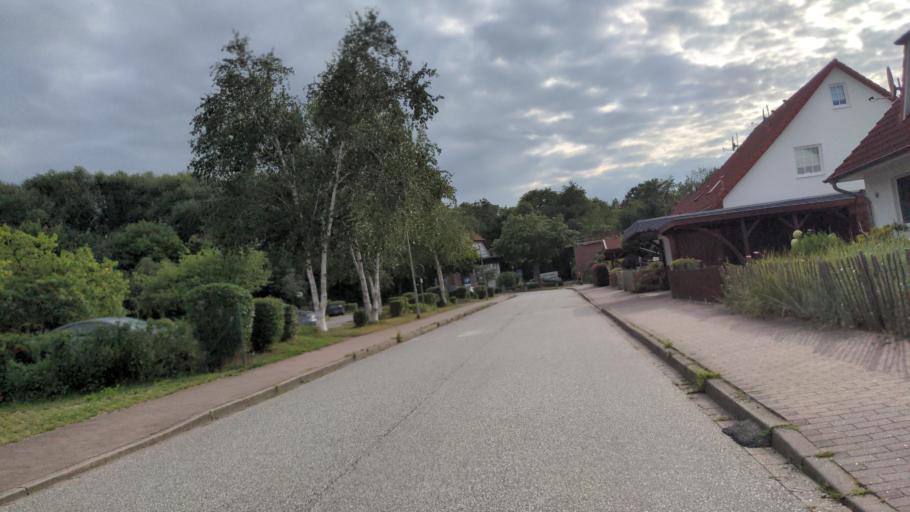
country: DE
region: Schleswig-Holstein
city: Neustadt in Holstein
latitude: 54.1054
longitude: 10.8003
